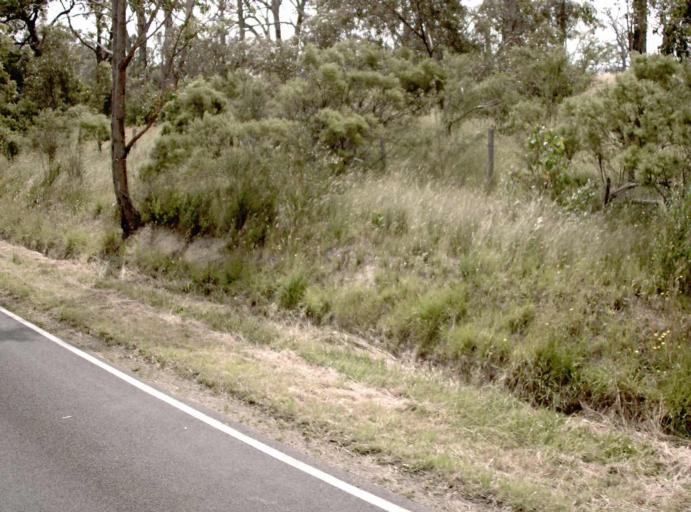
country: AU
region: Victoria
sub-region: Latrobe
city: Moe
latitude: -38.1342
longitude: 146.1472
